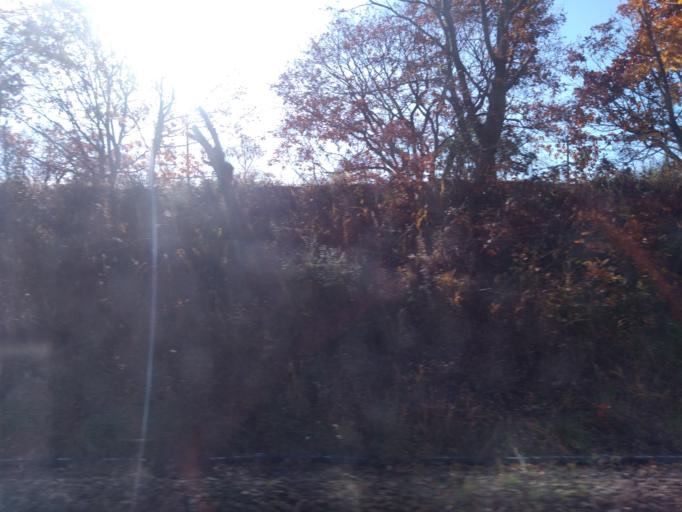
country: JP
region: Hokkaido
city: Chitose
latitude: 42.7894
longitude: 141.6974
